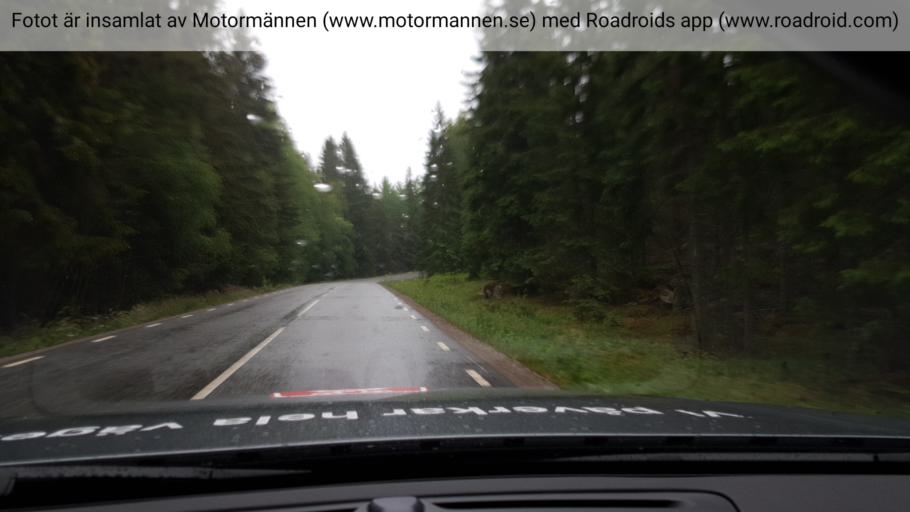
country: SE
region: Vaestmanland
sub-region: Norbergs Kommun
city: Norberg
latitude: 59.9747
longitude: 16.0207
